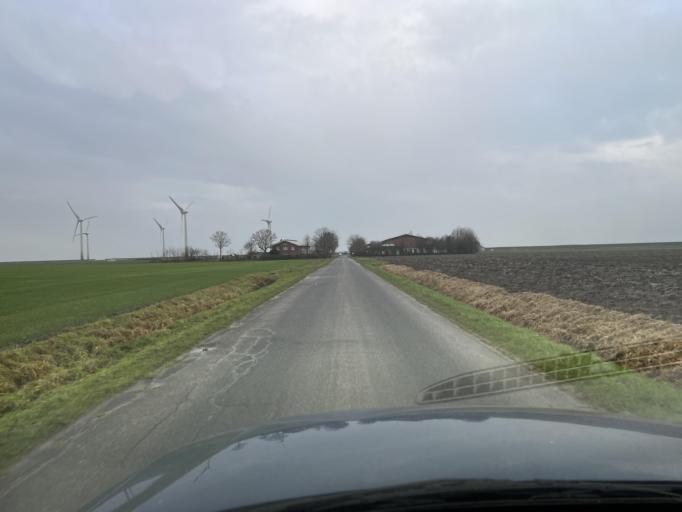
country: DE
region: Schleswig-Holstein
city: Hillgroven
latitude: 54.2196
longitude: 8.8695
